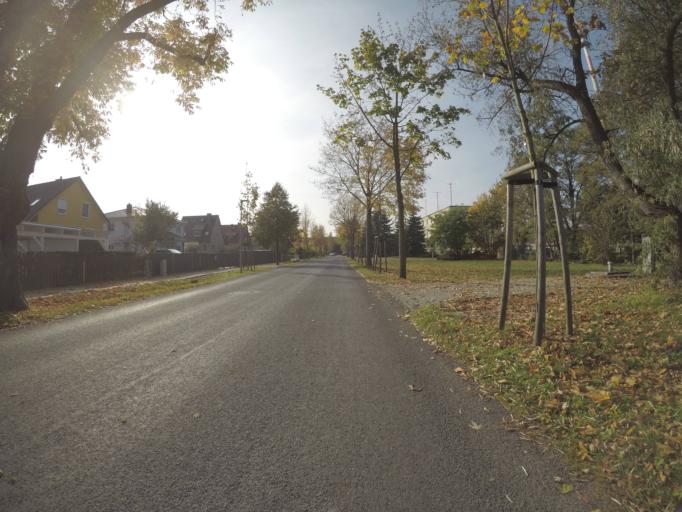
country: DE
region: Brandenburg
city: Schonefeld
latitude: 52.3953
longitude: 13.5249
